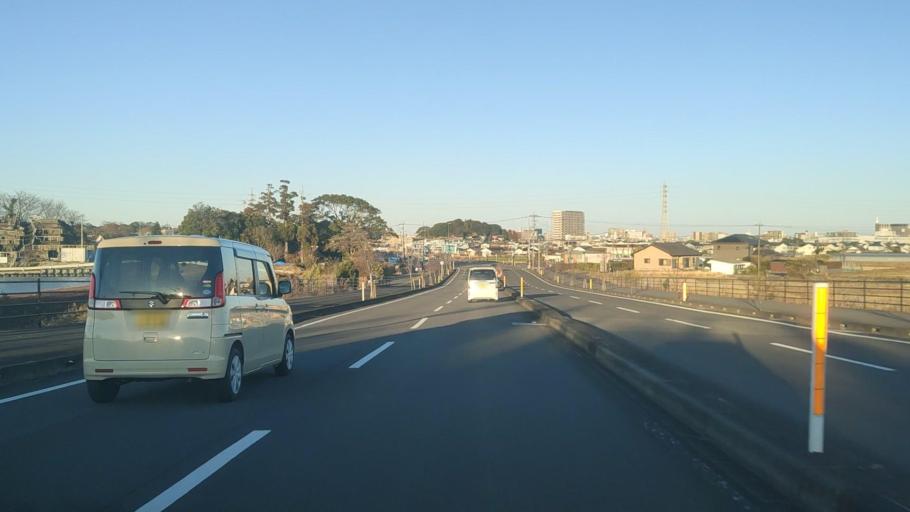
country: JP
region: Miyazaki
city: Miyazaki-shi
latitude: 31.8912
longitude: 131.4043
